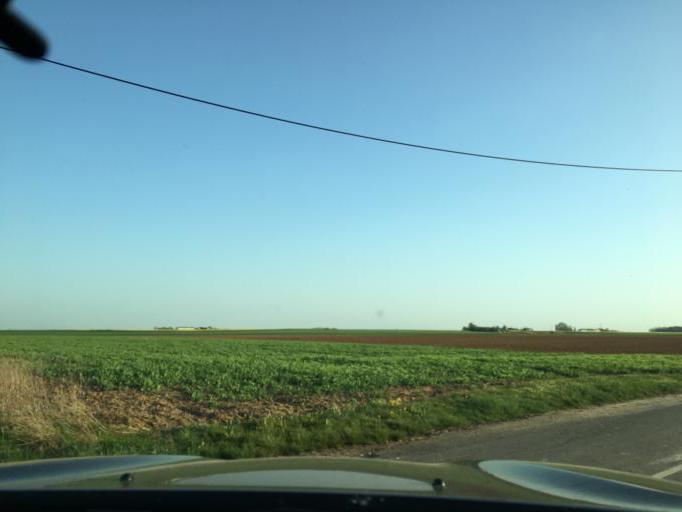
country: FR
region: Centre
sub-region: Departement du Loir-et-Cher
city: Ouzouer-le-Marche
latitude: 47.8448
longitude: 1.5337
